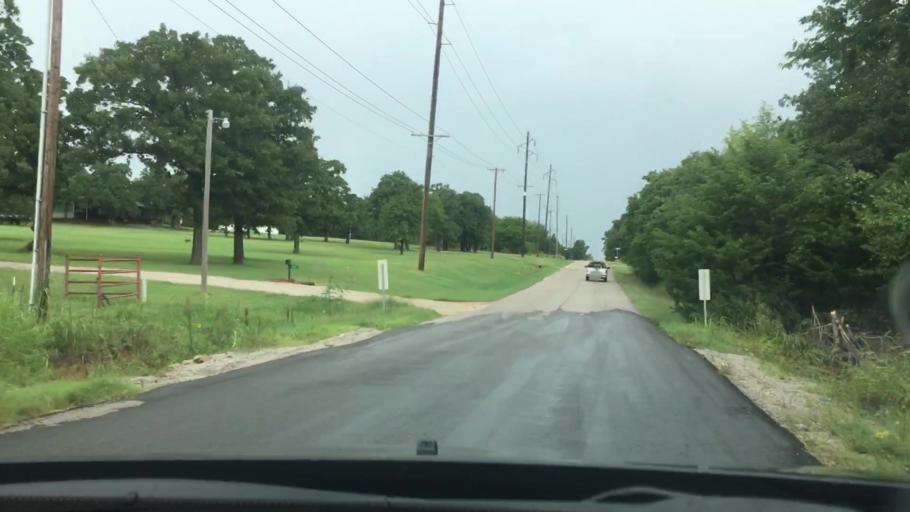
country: US
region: Oklahoma
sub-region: Carter County
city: Healdton
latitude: 34.2180
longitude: -97.4922
